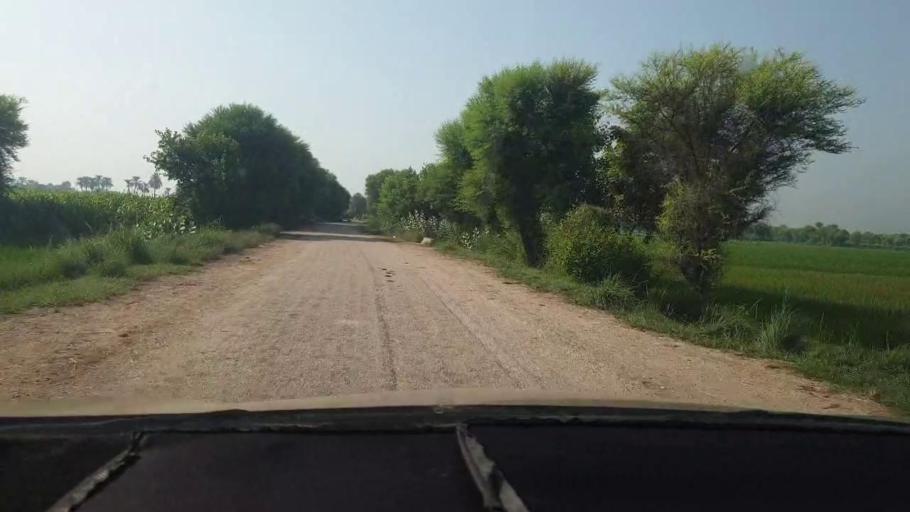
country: PK
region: Sindh
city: Kambar
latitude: 27.6165
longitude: 68.0905
